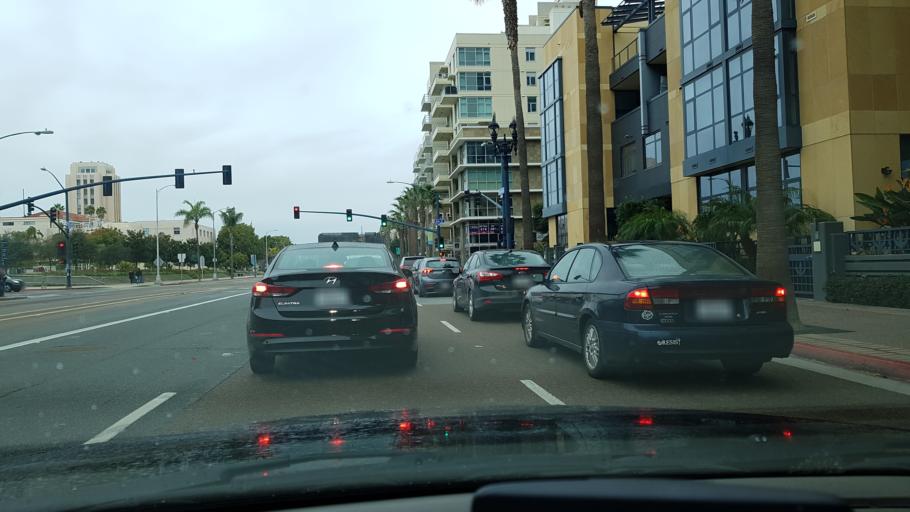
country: US
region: California
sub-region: San Diego County
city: San Diego
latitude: 32.7193
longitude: -117.1709
